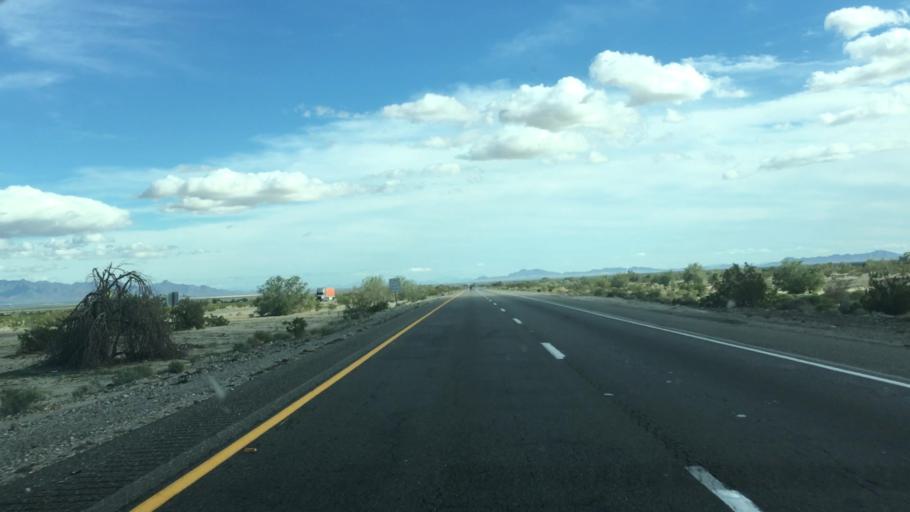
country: US
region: California
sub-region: Riverside County
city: Mesa Verde
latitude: 33.6544
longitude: -115.1492
